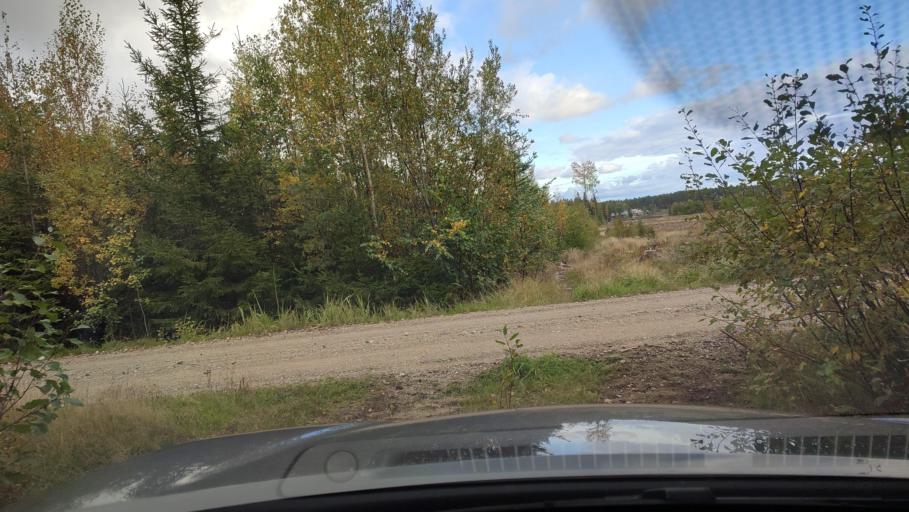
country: FI
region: Southern Ostrobothnia
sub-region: Suupohja
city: Karijoki
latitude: 62.2035
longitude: 21.6149
